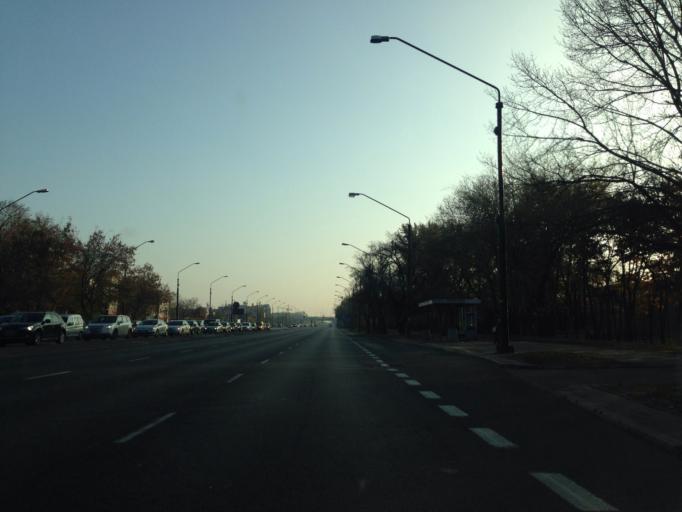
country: PL
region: Masovian Voivodeship
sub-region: Warszawa
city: Ursynow
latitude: 52.1472
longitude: 21.0176
